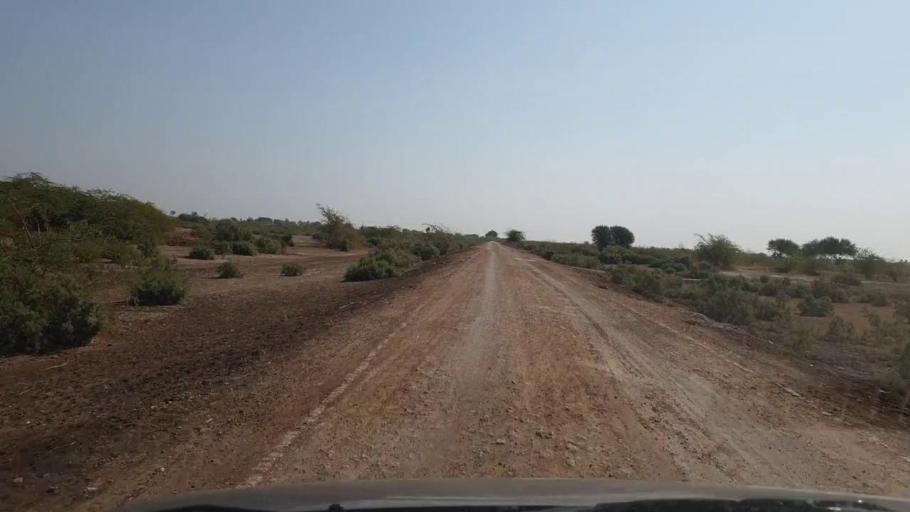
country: PK
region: Sindh
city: Samaro
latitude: 25.2489
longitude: 69.2828
